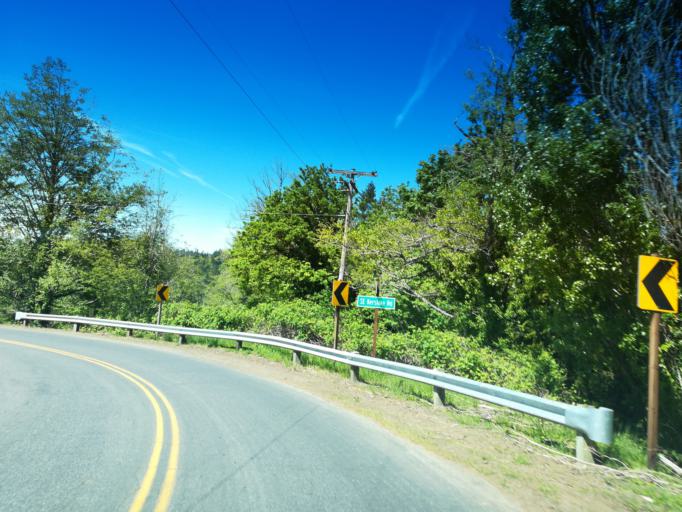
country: US
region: Oregon
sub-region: Multnomah County
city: Troutdale
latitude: 45.5118
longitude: -122.3521
